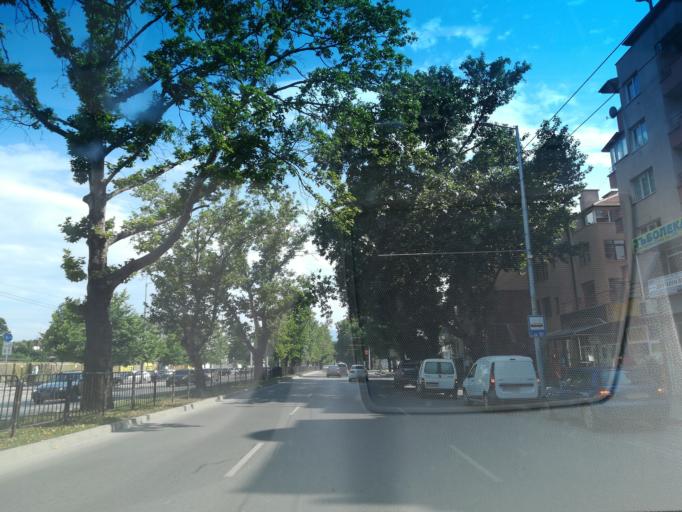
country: BG
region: Plovdiv
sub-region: Obshtina Plovdiv
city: Plovdiv
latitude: 42.1404
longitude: 24.7630
